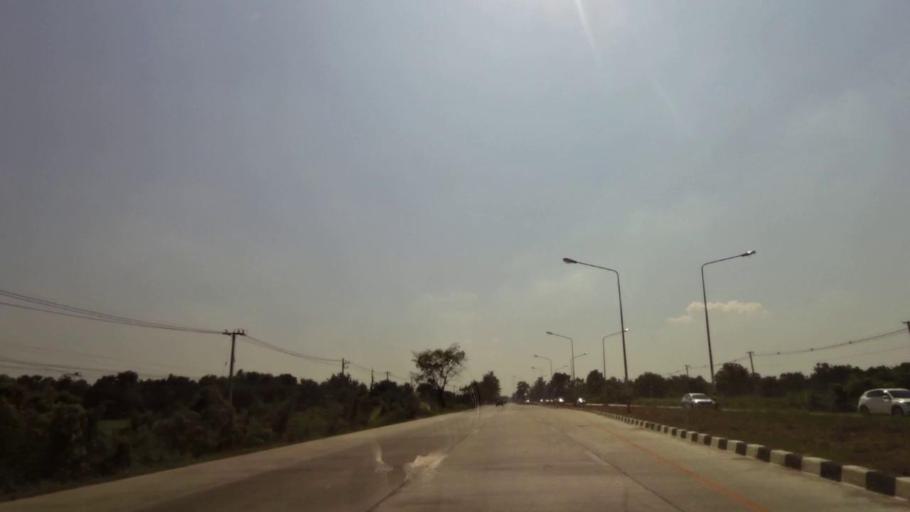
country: TH
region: Phichit
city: Bueng Na Rang
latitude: 16.2657
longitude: 100.1263
